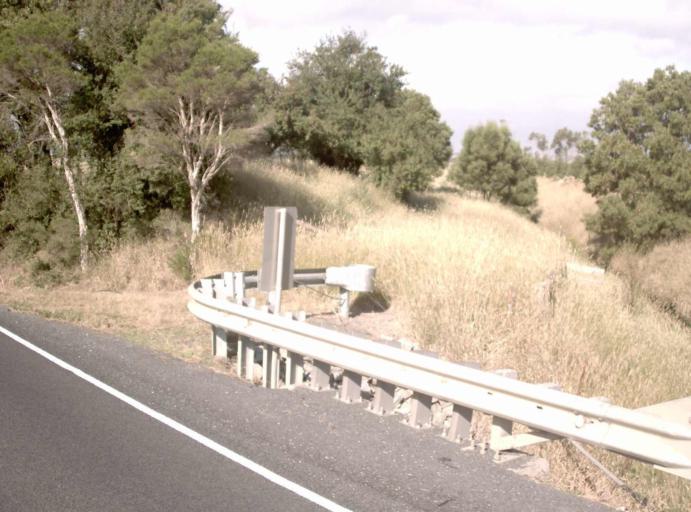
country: AU
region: Victoria
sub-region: Cardinia
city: Bunyip
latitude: -38.1748
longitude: 145.7173
